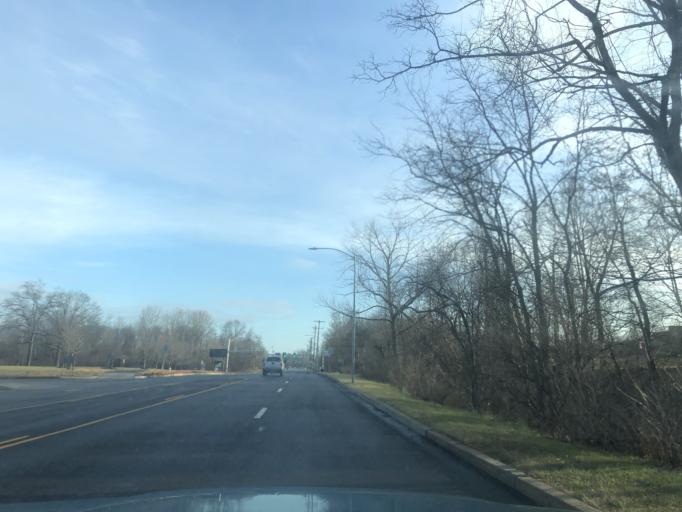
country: US
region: Pennsylvania
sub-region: Montgomery County
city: Dresher
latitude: 40.1380
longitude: -75.1762
